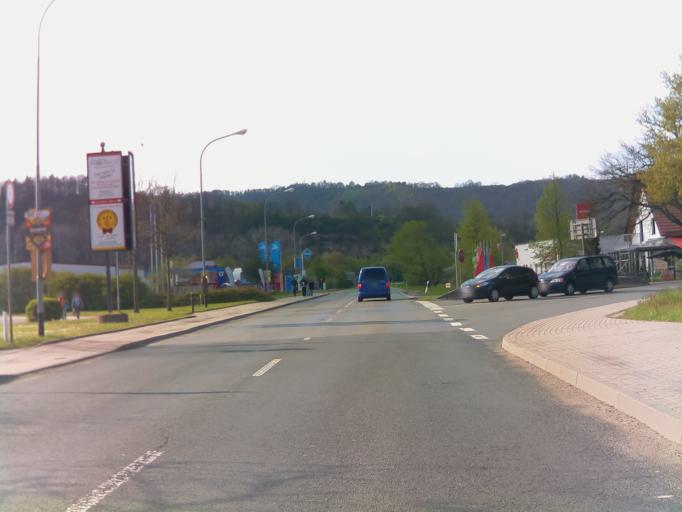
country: DE
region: Thuringia
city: Kaulsdorf
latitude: 50.6156
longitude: 11.4303
